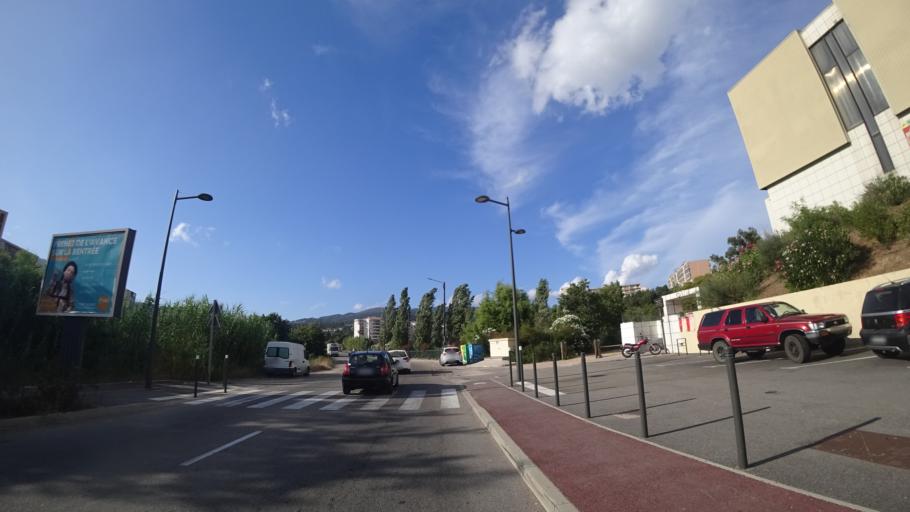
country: FR
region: Corsica
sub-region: Departement de la Corse-du-Sud
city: Ajaccio
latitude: 41.9364
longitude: 8.7427
